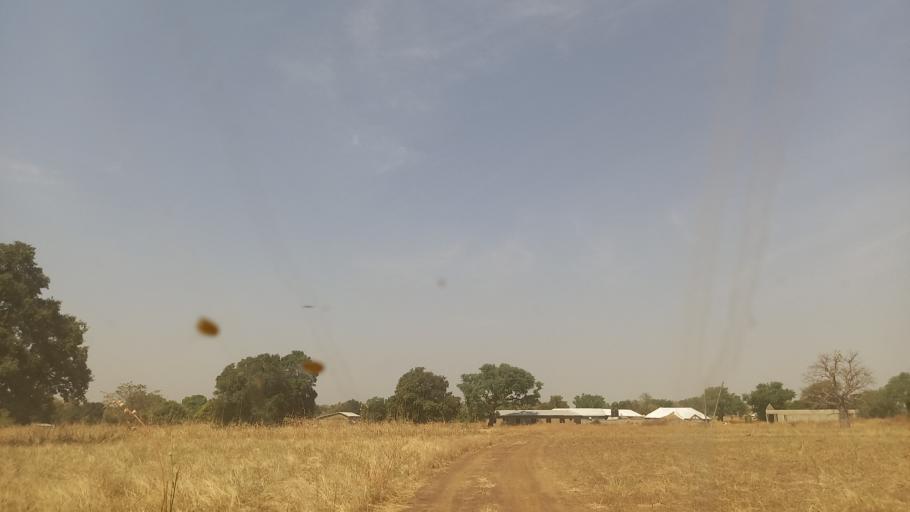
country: GH
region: Upper East
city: Navrongo
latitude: 10.8594
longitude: -1.0860
